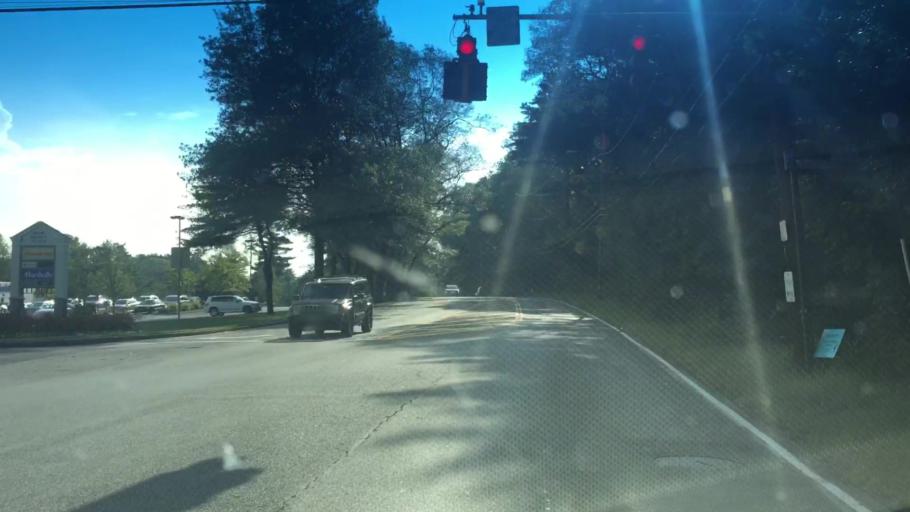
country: US
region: Massachusetts
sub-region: Norfolk County
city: Medfield
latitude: 42.1956
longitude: -71.2877
